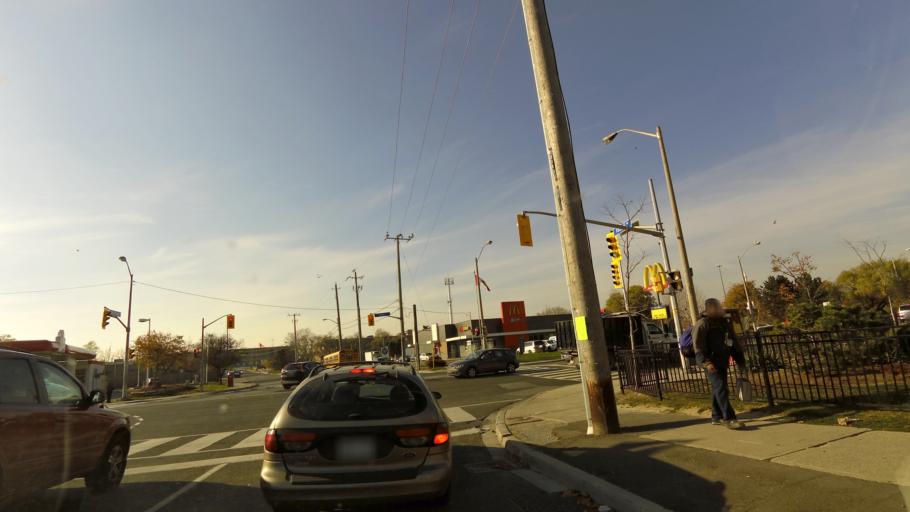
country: CA
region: Ontario
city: Etobicoke
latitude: 43.7154
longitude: -79.5069
